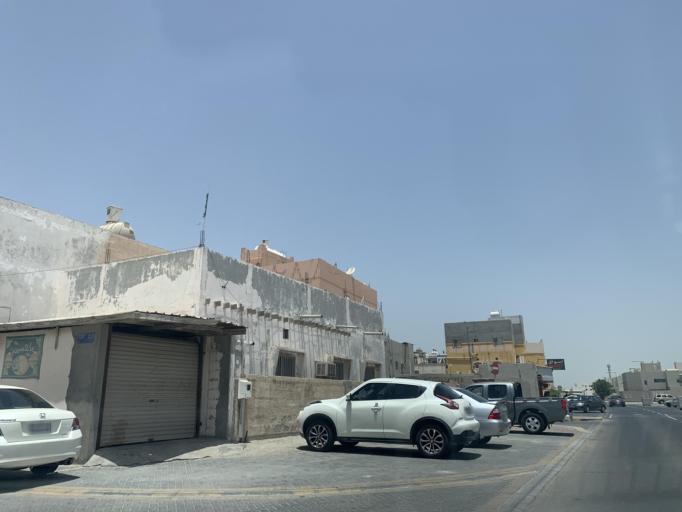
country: BH
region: Northern
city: Sitrah
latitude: 26.1575
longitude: 50.6238
